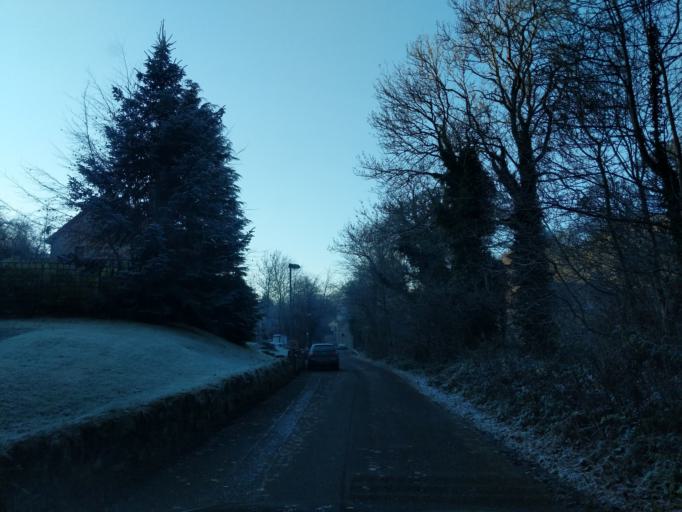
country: GB
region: Scotland
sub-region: Edinburgh
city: Colinton
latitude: 55.9058
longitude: -3.2702
